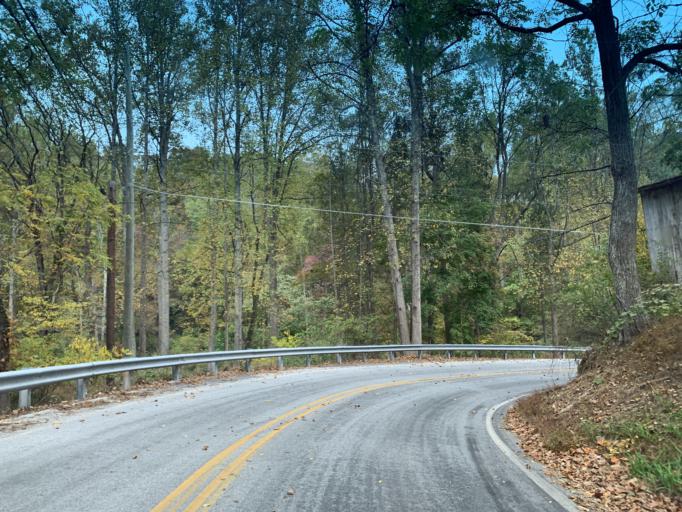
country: US
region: Pennsylvania
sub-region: York County
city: Stewartstown
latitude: 39.8261
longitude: -76.5123
